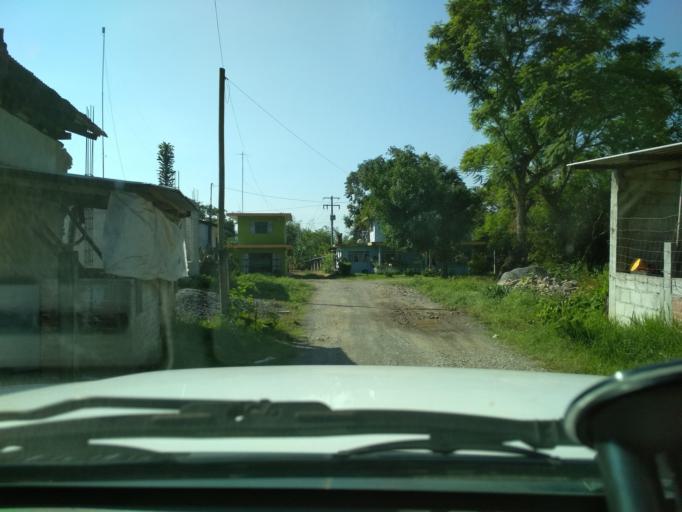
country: MX
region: Veracruz
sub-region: Chocaman
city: San Jose Neria
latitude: 18.9980
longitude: -97.0007
